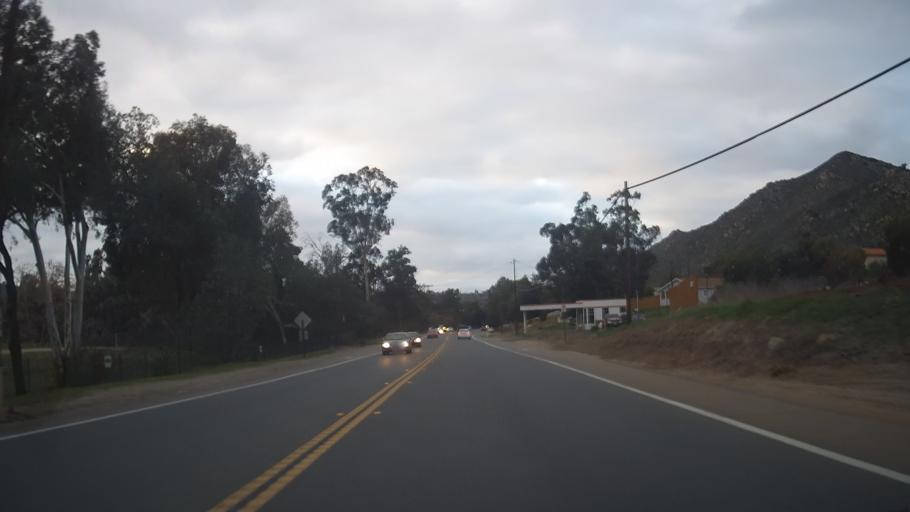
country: US
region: California
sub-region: San Diego County
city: Crest
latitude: 32.7797
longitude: -116.8705
